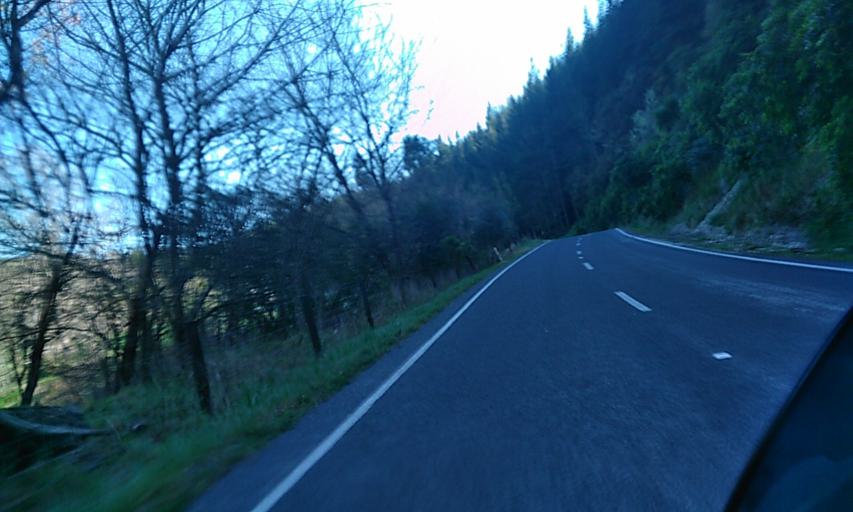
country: NZ
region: Gisborne
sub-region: Gisborne District
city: Gisborne
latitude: -38.5464
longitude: 178.0342
